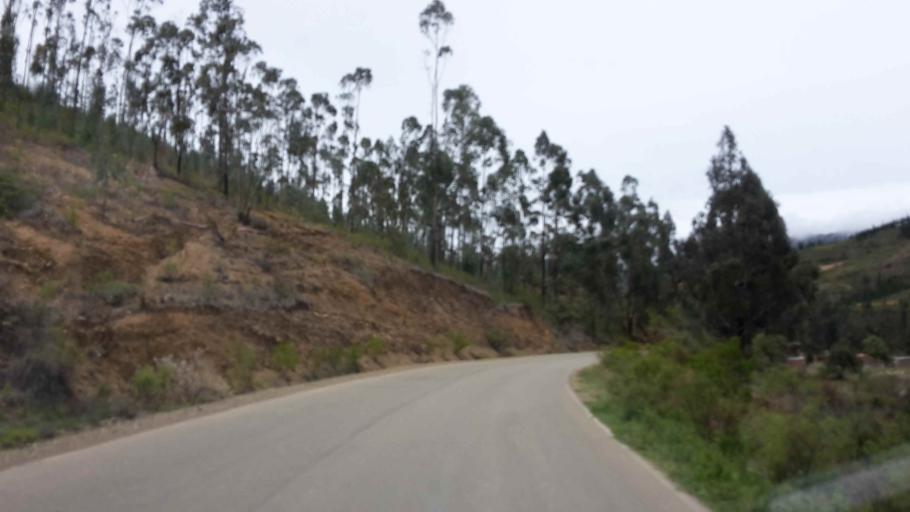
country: BO
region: Cochabamba
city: Totora
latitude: -17.6762
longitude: -65.2187
